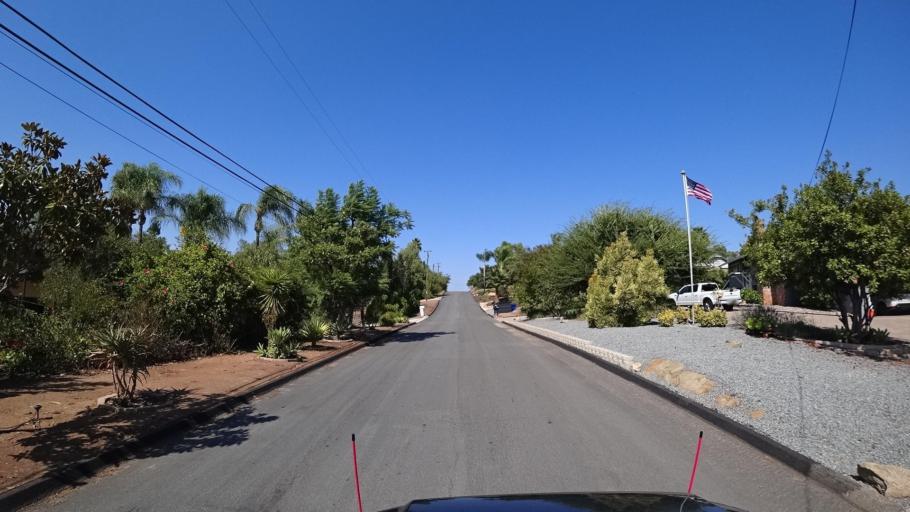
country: US
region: California
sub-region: San Diego County
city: Granite Hills
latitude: 32.7842
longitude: -116.8986
